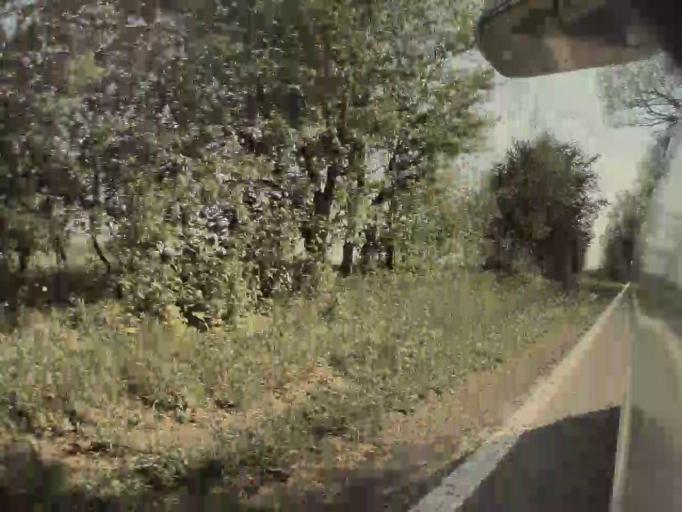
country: BE
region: Wallonia
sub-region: Province de Namur
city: Hamois
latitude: 50.2961
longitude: 5.2085
